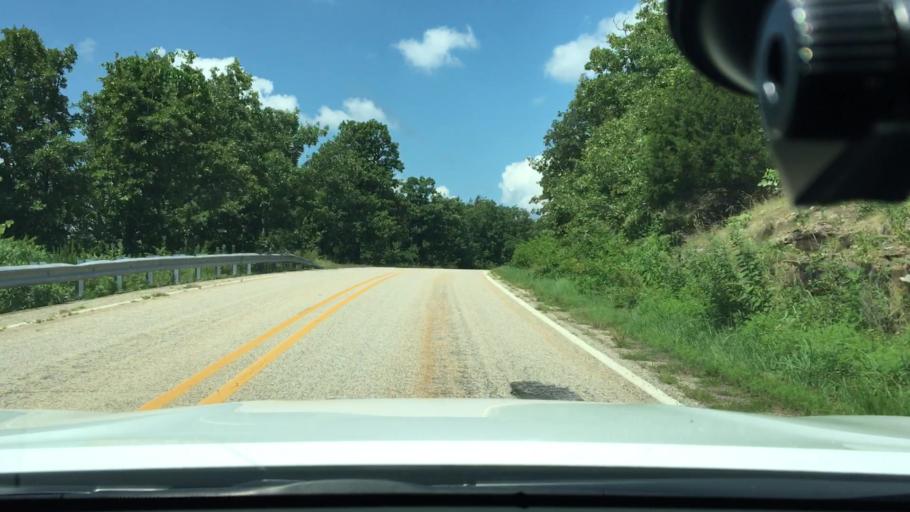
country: US
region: Arkansas
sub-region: Logan County
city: Paris
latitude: 35.1755
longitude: -93.5925
